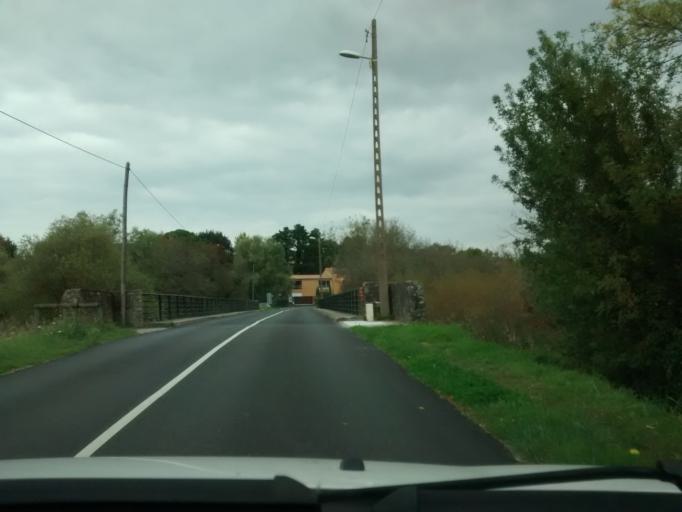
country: FR
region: Pays de la Loire
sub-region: Departement de la Loire-Atlantique
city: Le Pellerin
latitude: 47.2082
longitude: -1.7492
